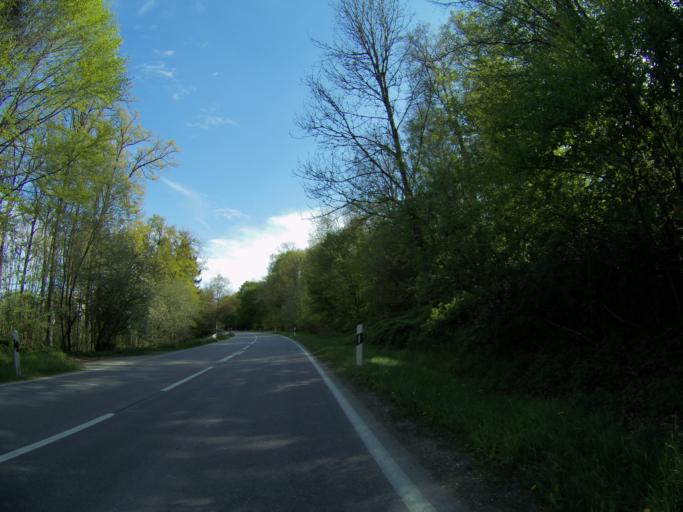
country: DE
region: Bavaria
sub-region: Upper Bavaria
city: Freising
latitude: 48.4082
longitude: 11.7166
